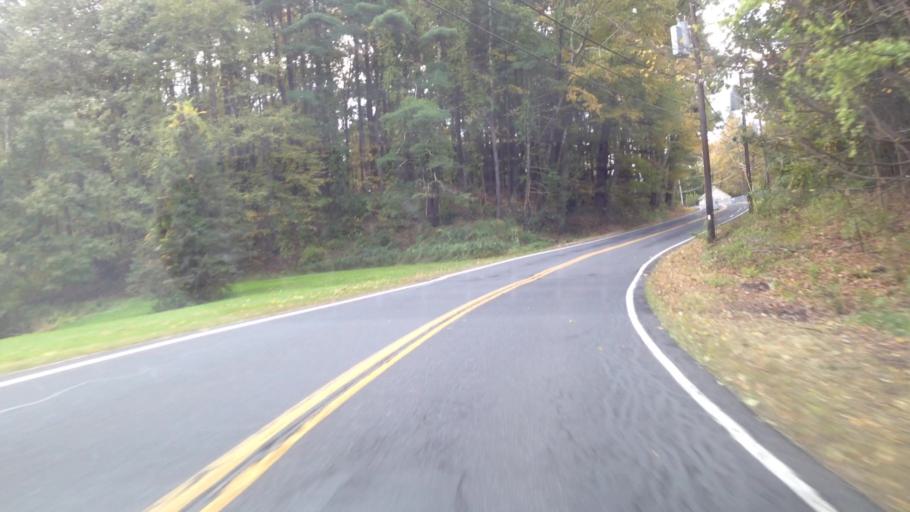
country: US
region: New York
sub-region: Ulster County
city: Tillson
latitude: 41.8345
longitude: -74.0778
